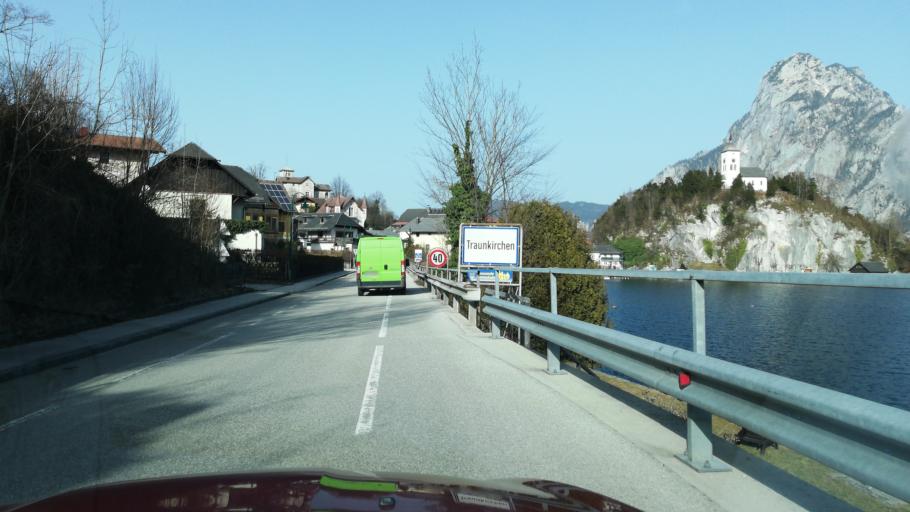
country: AT
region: Upper Austria
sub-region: Politischer Bezirk Gmunden
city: Ebensee
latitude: 47.8425
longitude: 13.7884
